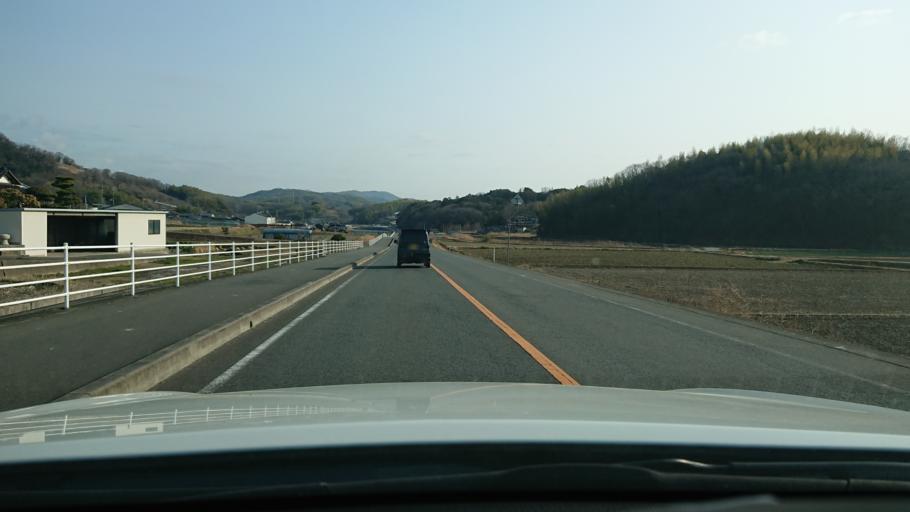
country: JP
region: Okayama
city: Kurashiki
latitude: 34.6020
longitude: 133.7019
